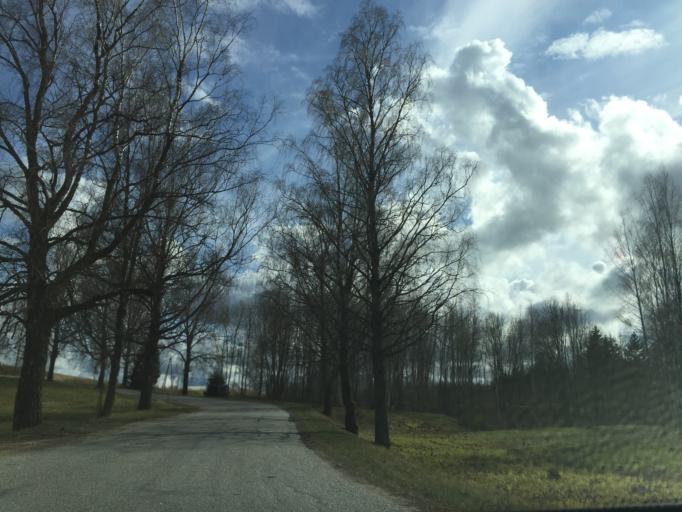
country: LV
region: Limbazu Rajons
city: Limbazi
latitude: 57.5976
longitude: 24.8268
